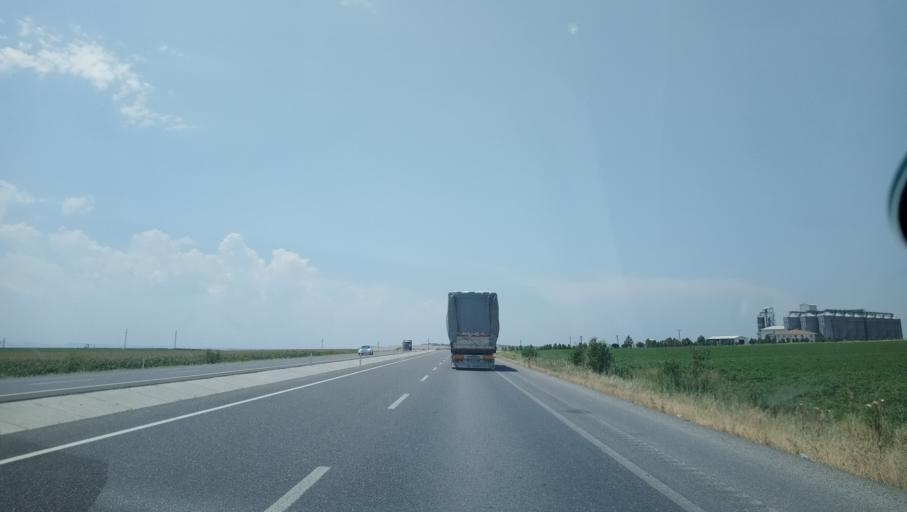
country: TR
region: Diyarbakir
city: Salat
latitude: 37.8552
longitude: 40.8581
